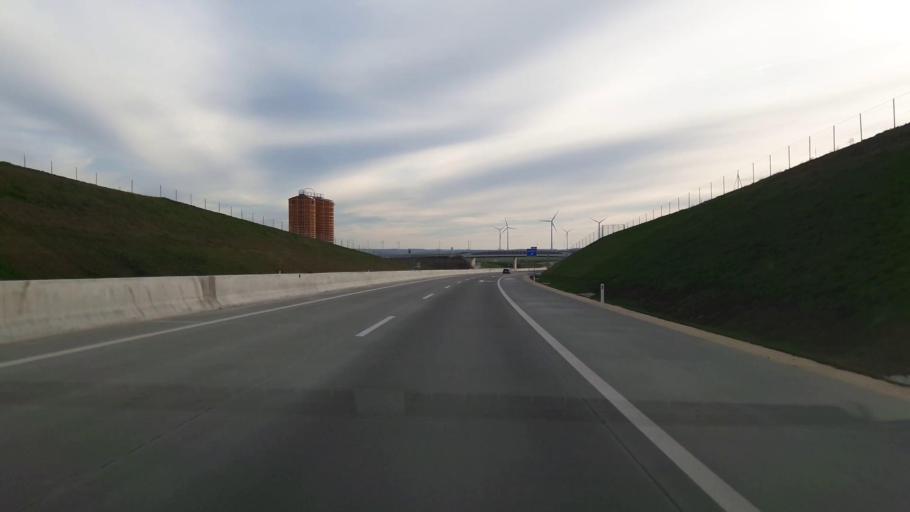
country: AT
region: Lower Austria
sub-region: Politischer Bezirk Mistelbach
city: Herrnbaumgarten
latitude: 48.6565
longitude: 16.6899
